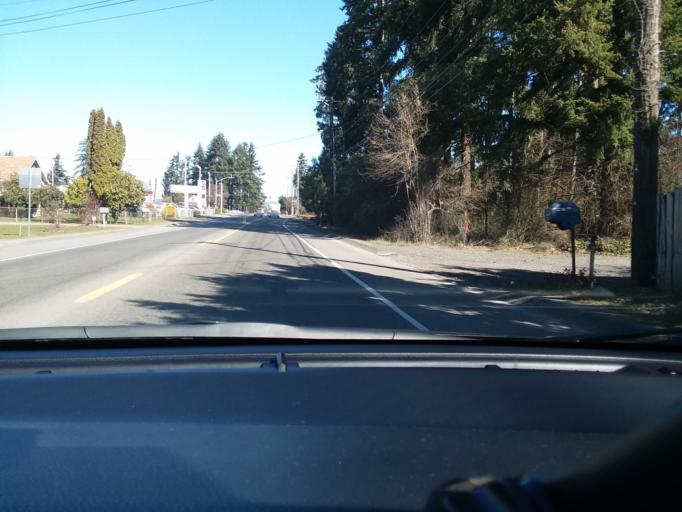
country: US
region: Washington
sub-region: Pierce County
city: Waller
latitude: 47.1901
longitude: -122.3573
